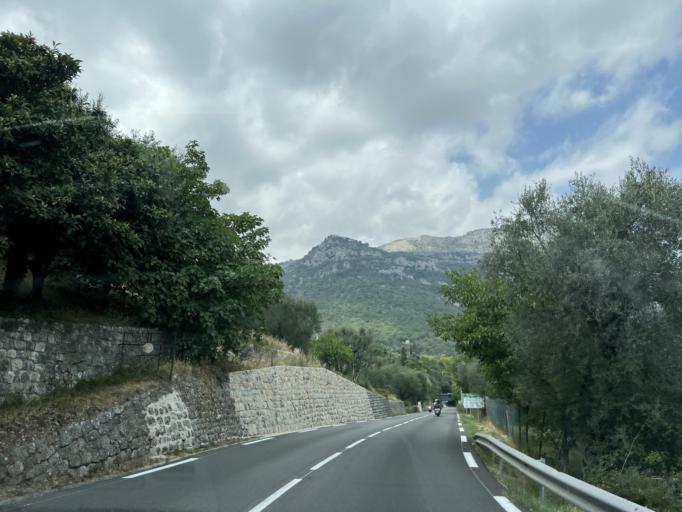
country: FR
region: Provence-Alpes-Cote d'Azur
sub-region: Departement des Alpes-Maritimes
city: Le Rouret
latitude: 43.7065
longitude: 6.9907
